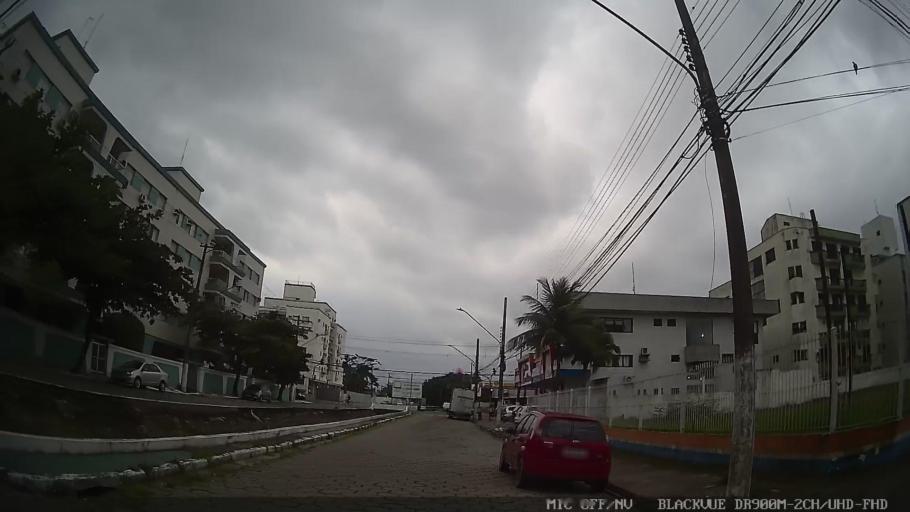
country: BR
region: Sao Paulo
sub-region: Guaruja
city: Guaruja
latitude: -24.0082
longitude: -46.2745
